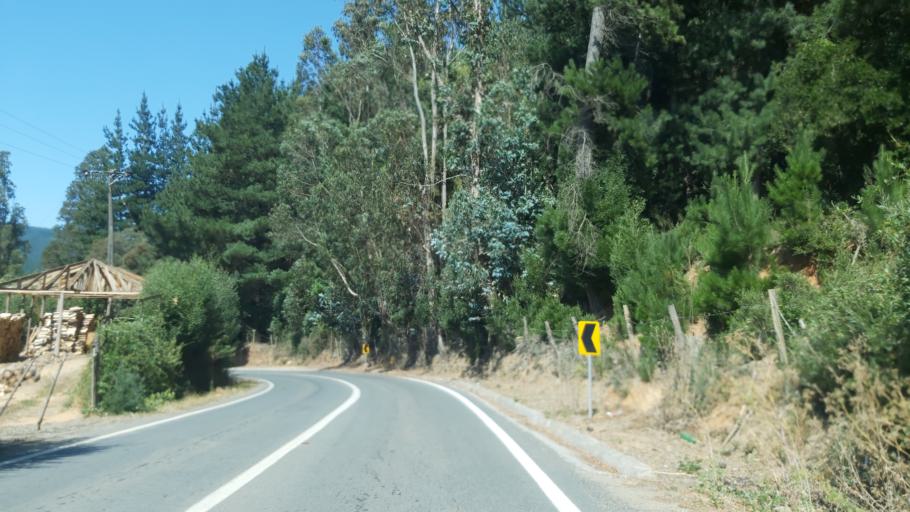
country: CL
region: Biobio
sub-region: Provincia de Concepcion
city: Tome
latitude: -36.5548
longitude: -72.8699
